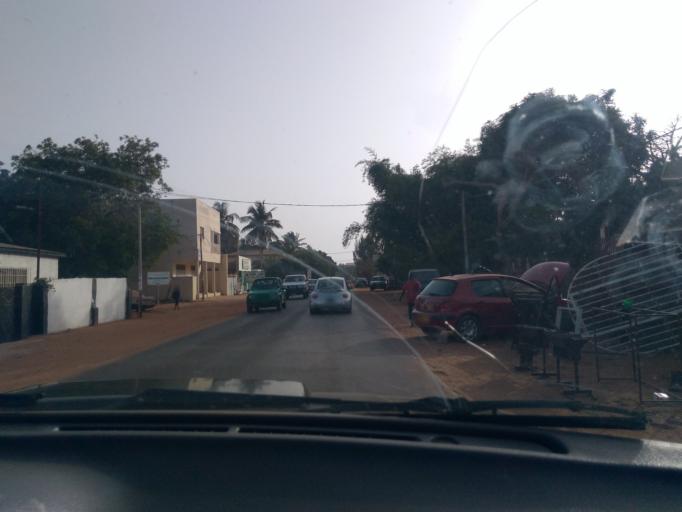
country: GM
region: Banjul
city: Bakau
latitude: 13.4695
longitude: -16.6880
